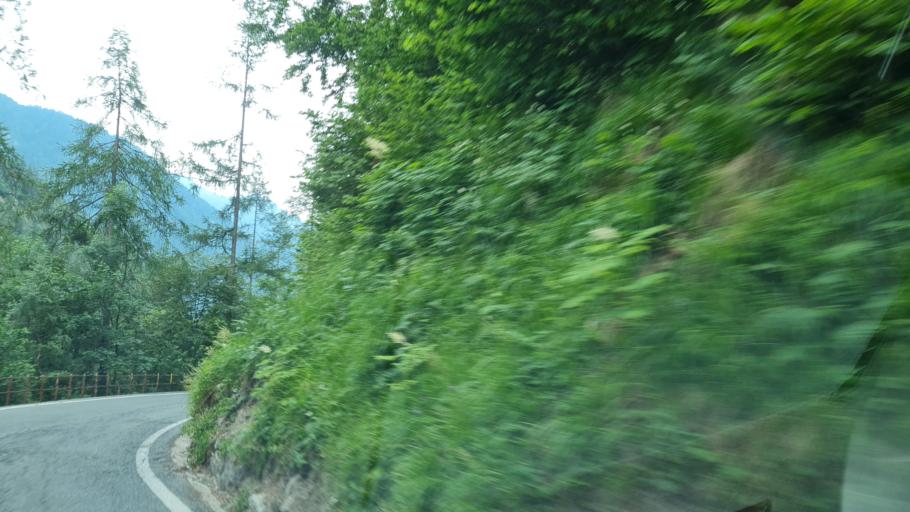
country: IT
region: Piedmont
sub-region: Provincia di Torino
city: Valprato Soana
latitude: 45.5350
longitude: 7.5401
